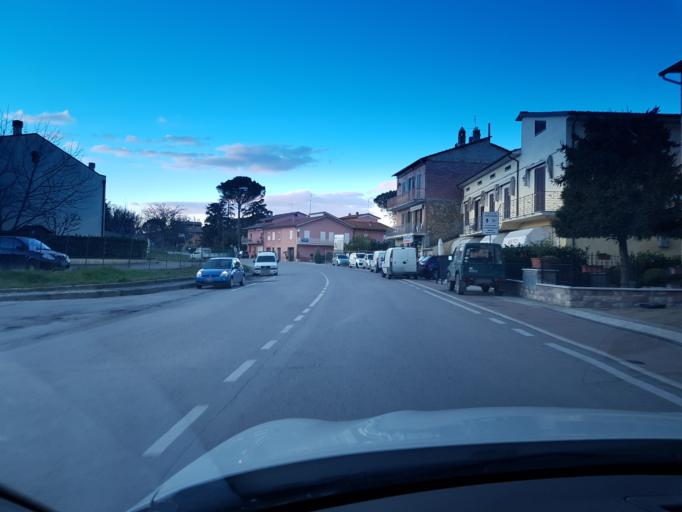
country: IT
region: Umbria
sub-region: Provincia di Perugia
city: Torgiano
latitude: 43.0271
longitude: 12.4447
